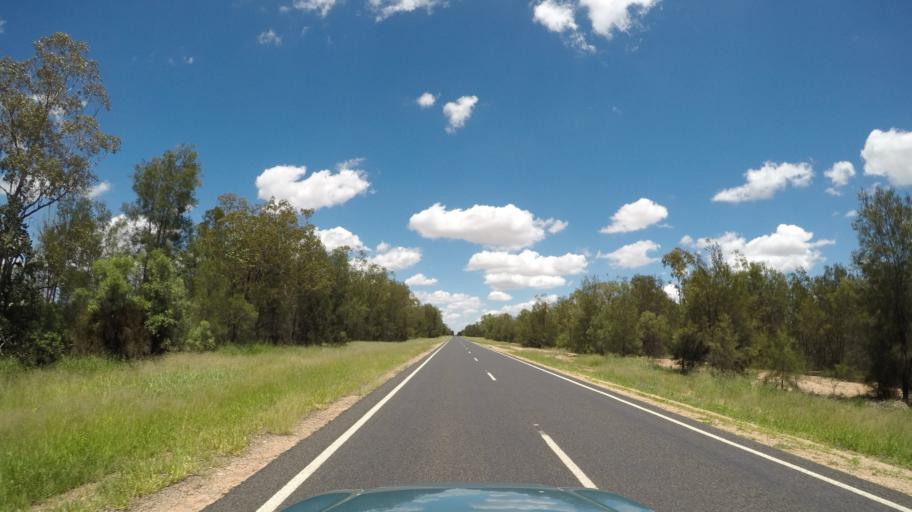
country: AU
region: Queensland
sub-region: Goondiwindi
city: Goondiwindi
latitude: -28.1629
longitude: 150.6184
